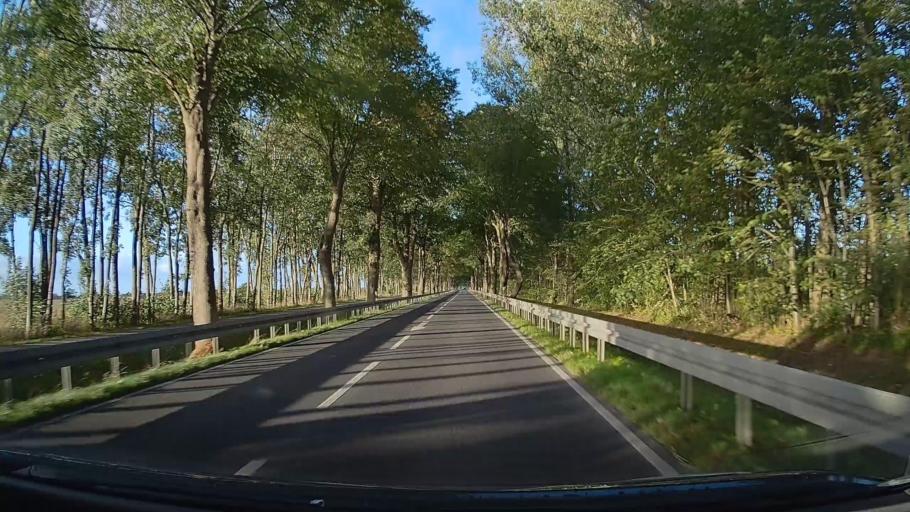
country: DE
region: Mecklenburg-Vorpommern
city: Wendorf
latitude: 54.2746
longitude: 13.0408
